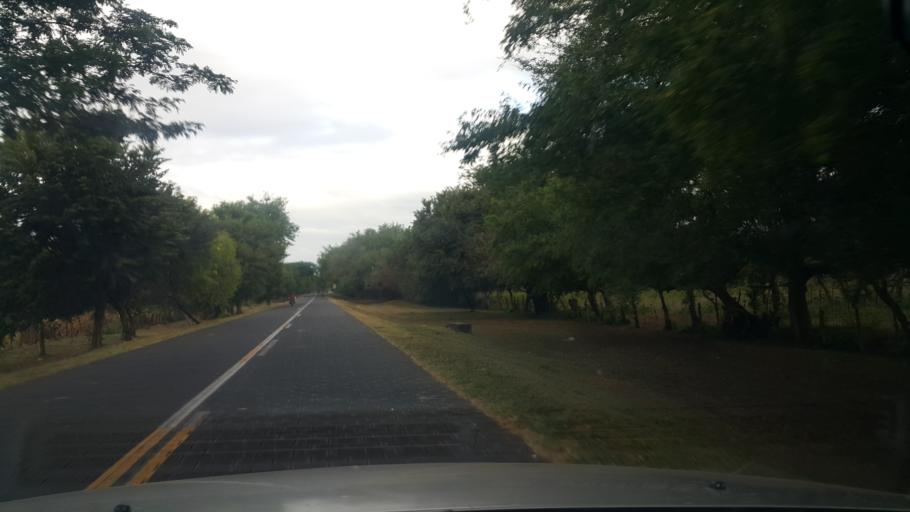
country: NI
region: Rivas
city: Moyogalpa
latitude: 11.5190
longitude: -85.7050
